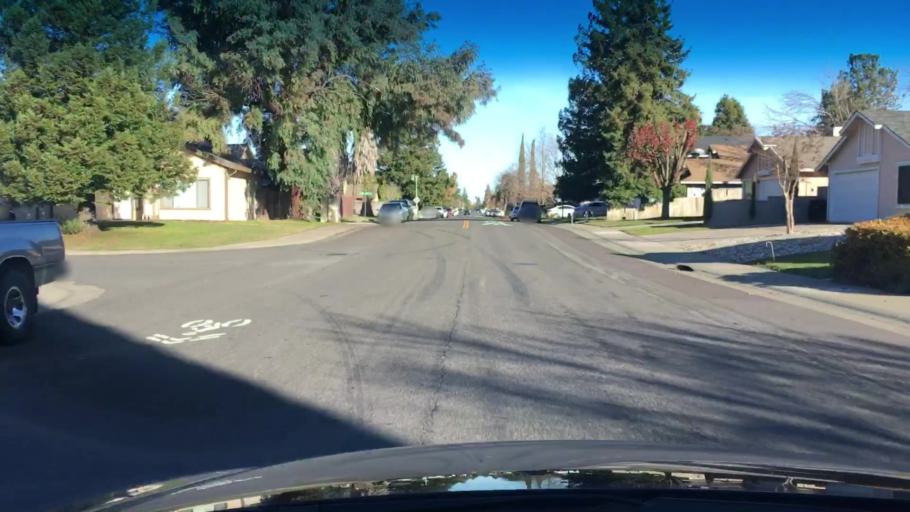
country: US
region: California
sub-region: Sacramento County
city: Laguna
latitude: 38.4483
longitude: -121.4341
